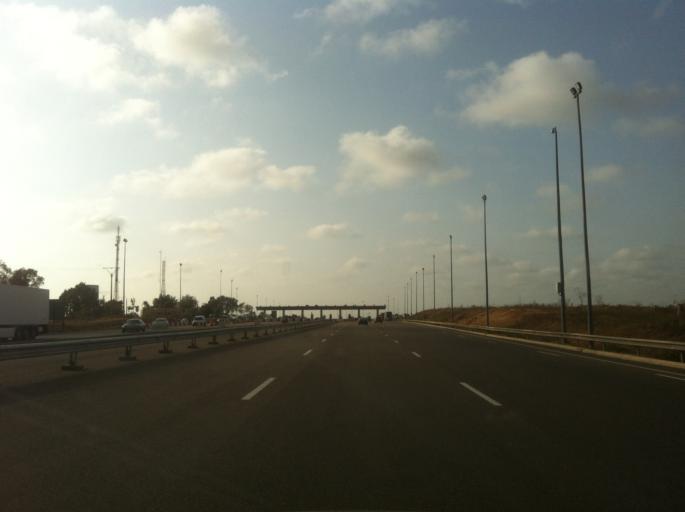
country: MA
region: Gharb-Chrarda-Beni Hssen
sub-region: Kenitra Province
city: Kenitra
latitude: 34.2273
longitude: -6.5270
